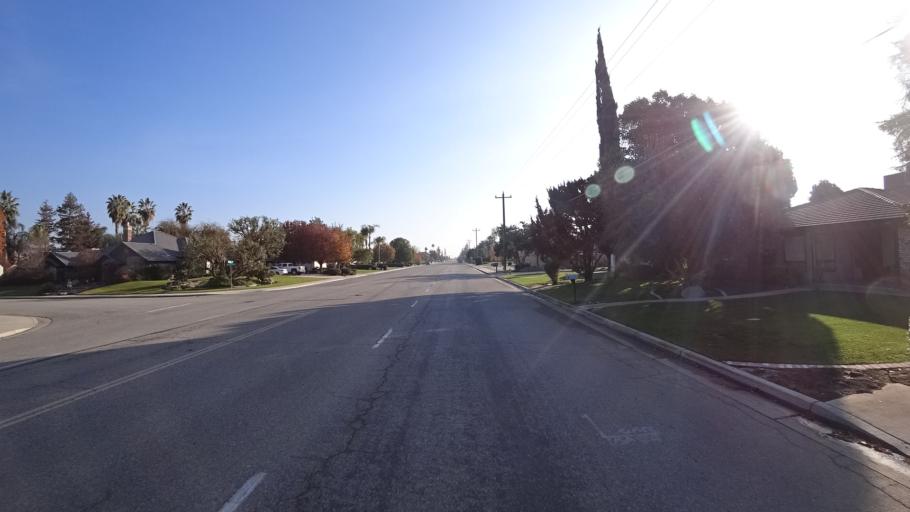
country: US
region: California
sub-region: Kern County
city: Rosedale
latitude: 35.3763
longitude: -119.1407
